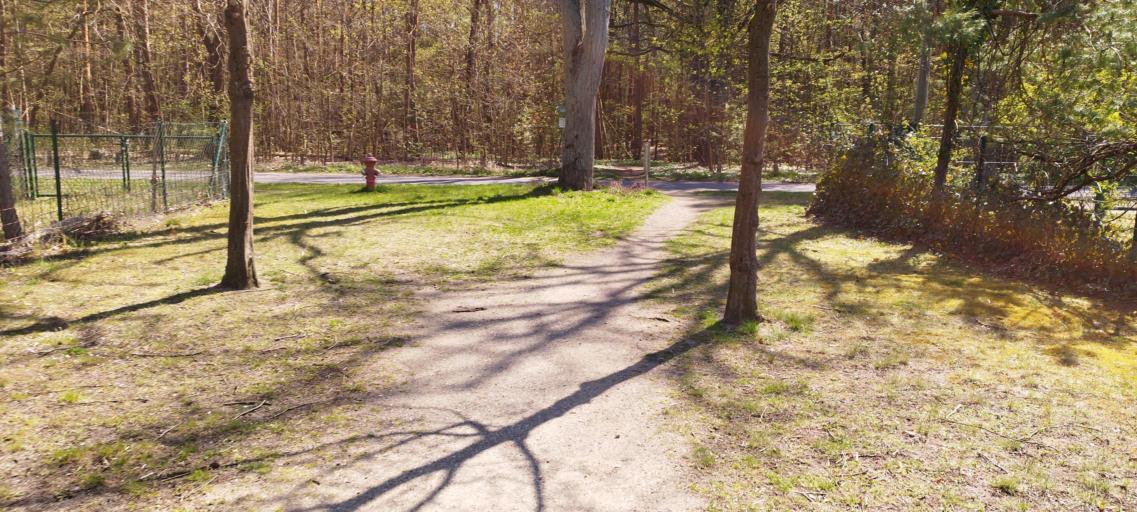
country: DE
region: Brandenburg
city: Grunheide
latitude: 52.4272
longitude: 13.8419
